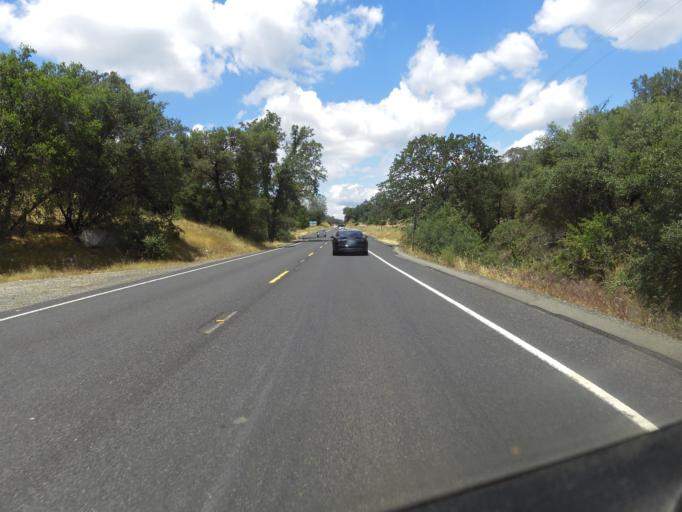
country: US
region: California
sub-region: Madera County
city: Coarsegold
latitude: 37.2229
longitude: -119.7076
